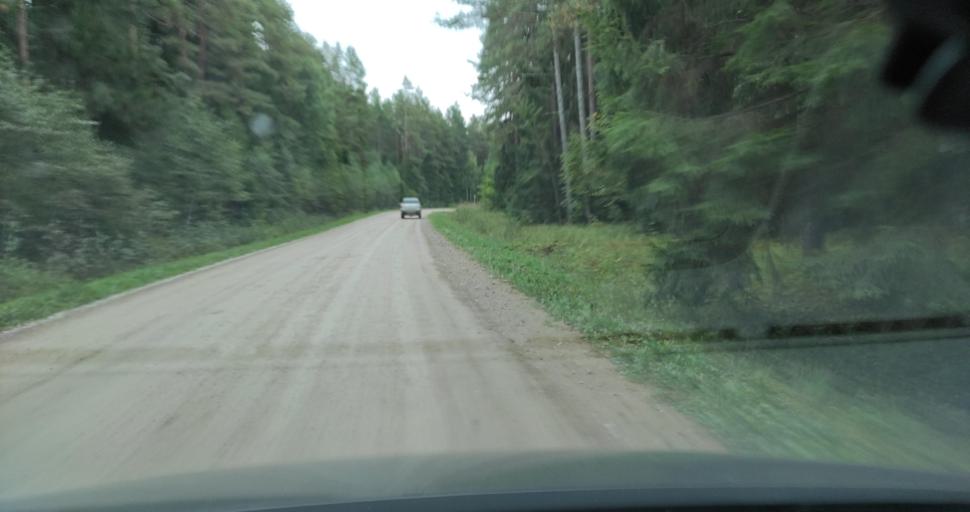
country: LV
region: Talsu Rajons
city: Stende
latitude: 57.0358
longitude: 22.3201
